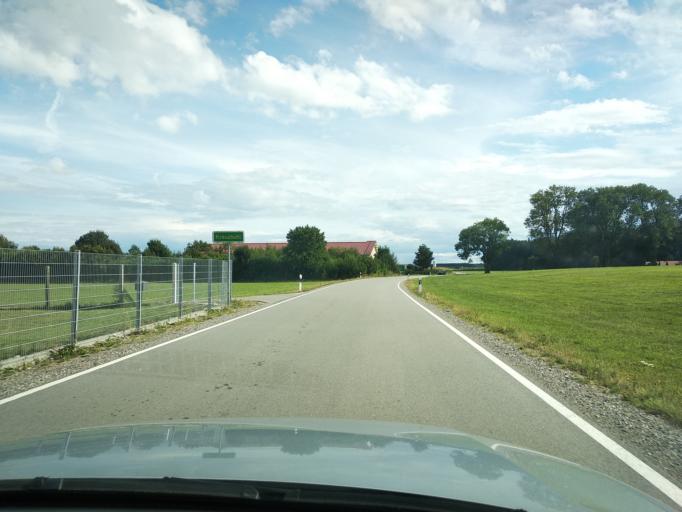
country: DE
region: Bavaria
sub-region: Swabia
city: Wolfertschwenden
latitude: 47.8779
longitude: 10.2353
